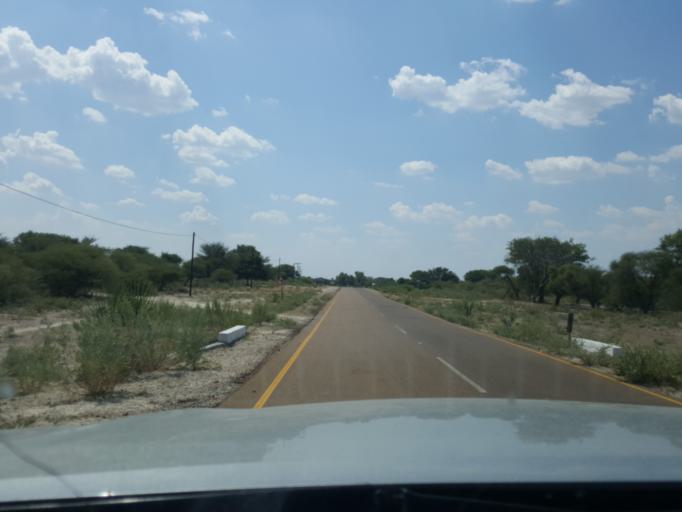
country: BW
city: Nokaneng
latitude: -19.6755
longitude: 22.1952
